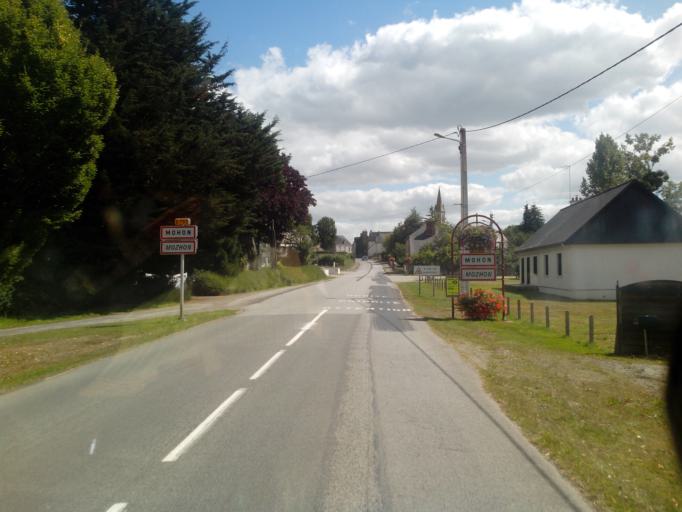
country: FR
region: Brittany
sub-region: Departement des Cotes-d'Armor
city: Plumieux
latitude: 48.0552
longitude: -2.5286
